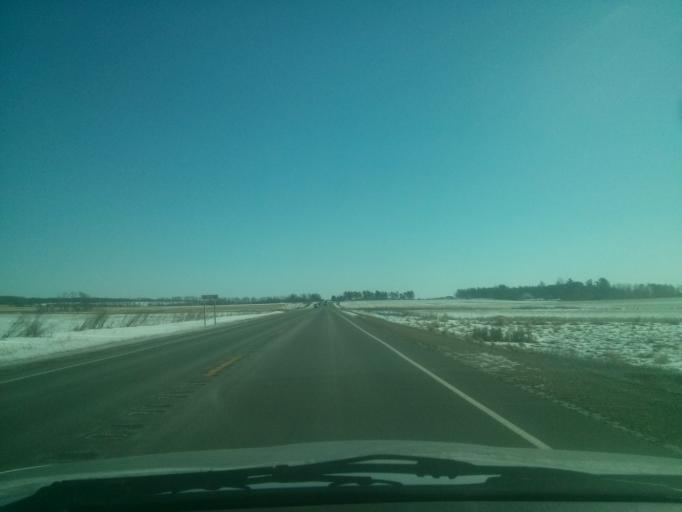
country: US
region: Wisconsin
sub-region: Polk County
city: Clear Lake
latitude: 45.1364
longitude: -92.3613
